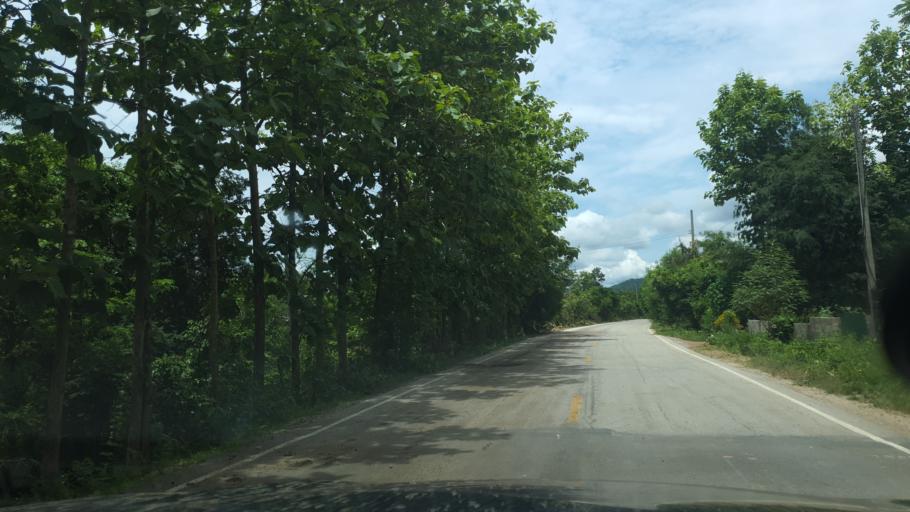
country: TH
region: Lampang
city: Sop Prap
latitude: 17.9200
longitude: 99.4049
